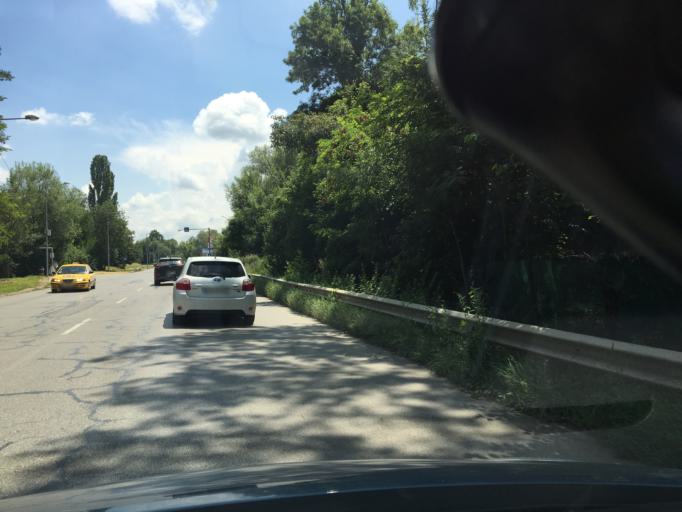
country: BG
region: Sofia-Capital
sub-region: Stolichna Obshtina
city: Sofia
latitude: 42.6607
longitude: 23.3050
